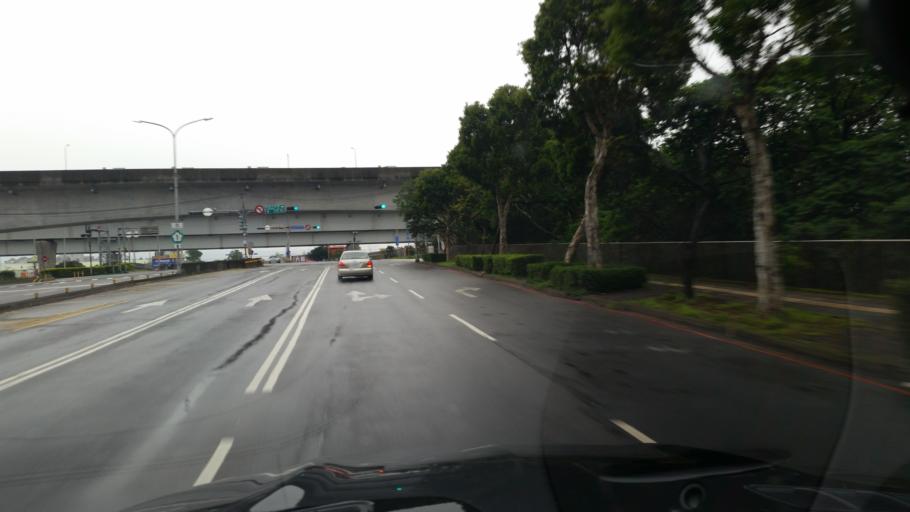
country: TW
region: Taiwan
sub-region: Taoyuan
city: Taoyuan
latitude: 25.0668
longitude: 121.3554
